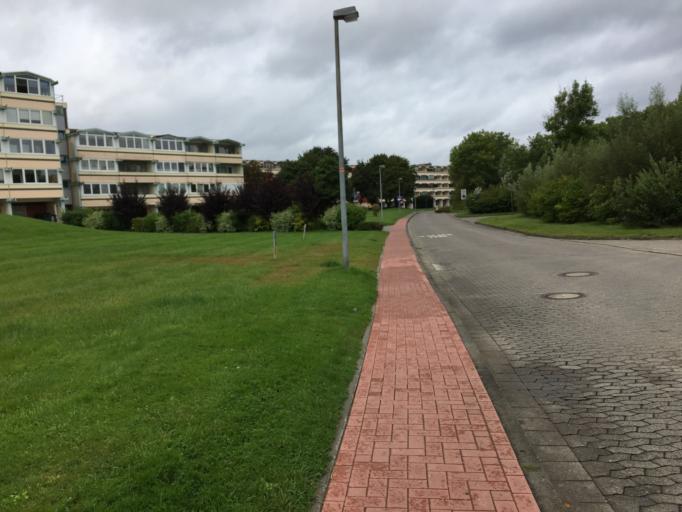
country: DE
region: Schleswig-Holstein
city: Wisch
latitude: 54.4190
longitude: 10.3708
